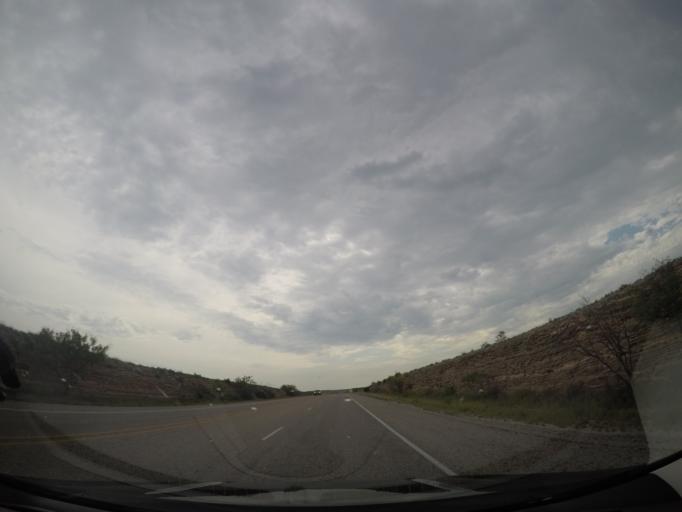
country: US
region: Texas
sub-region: Val Verde County
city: Cienegas Terrace
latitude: 29.7092
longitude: -101.2866
